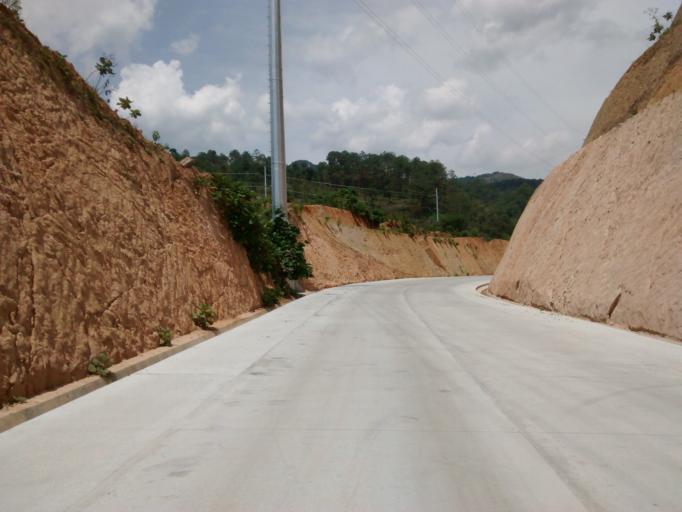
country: GT
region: Sacatepequez
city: Santo Domingo Xenacoj
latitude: 14.6911
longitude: -90.7111
